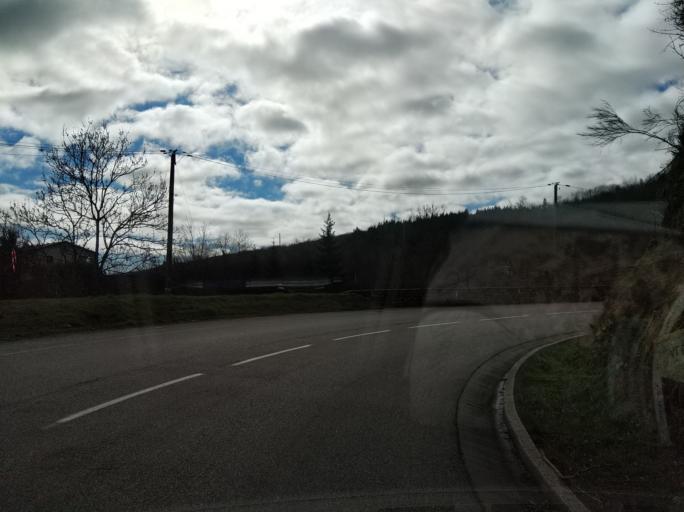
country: FR
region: Rhone-Alpes
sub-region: Departement de la Loire
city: Pelussin
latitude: 45.4151
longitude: 4.6684
